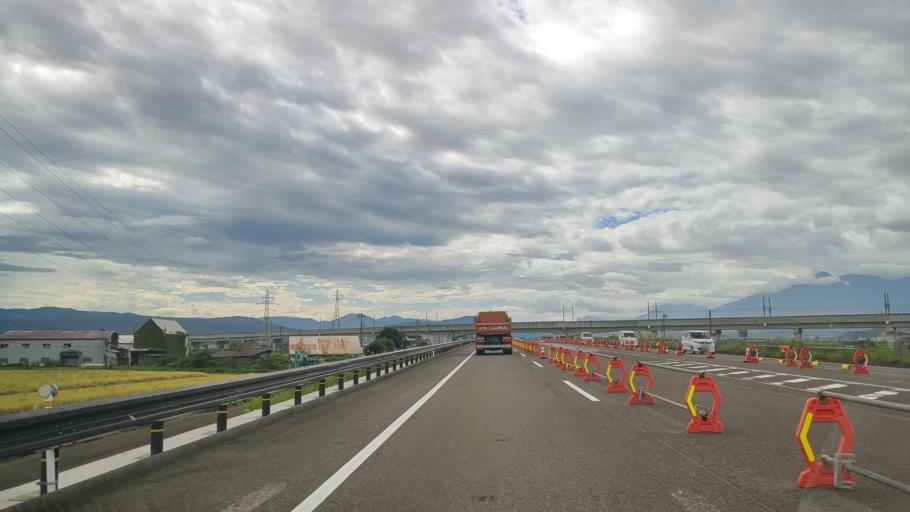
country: JP
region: Niigata
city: Arai
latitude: 37.0711
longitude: 138.2644
